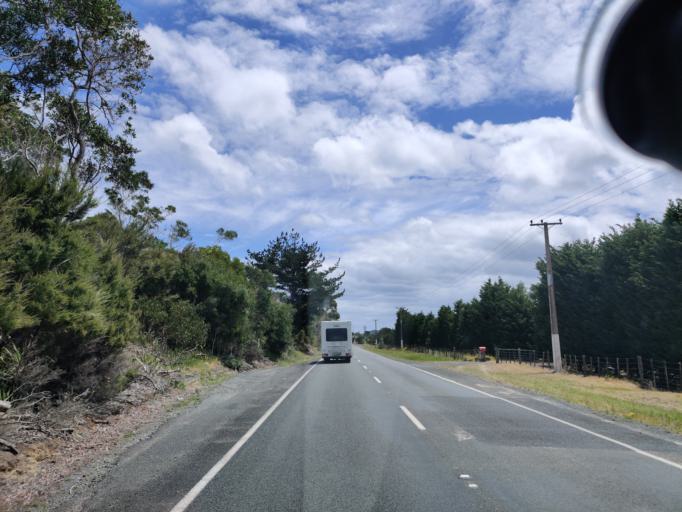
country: NZ
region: Northland
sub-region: Far North District
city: Kaitaia
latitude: -34.7821
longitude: 173.0959
